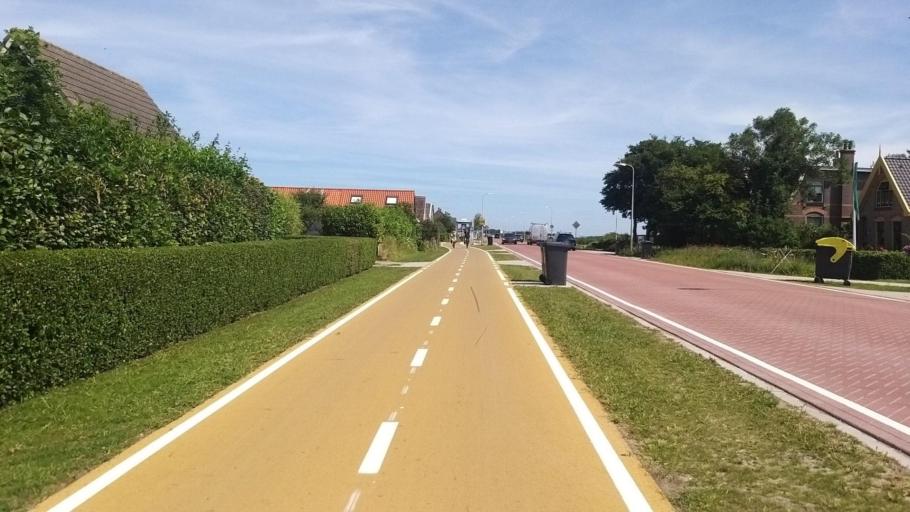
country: NL
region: North Holland
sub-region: Gemeente Texel
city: Den Burg
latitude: 53.1116
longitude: 4.8189
